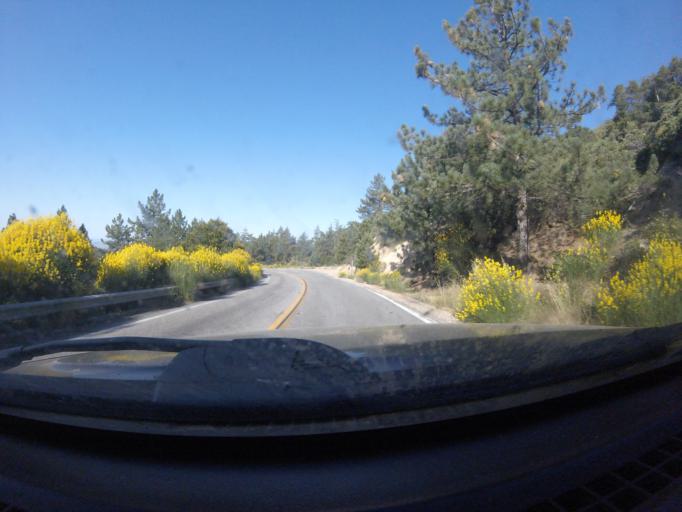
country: US
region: California
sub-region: San Bernardino County
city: Running Springs
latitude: 34.1934
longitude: -117.1531
